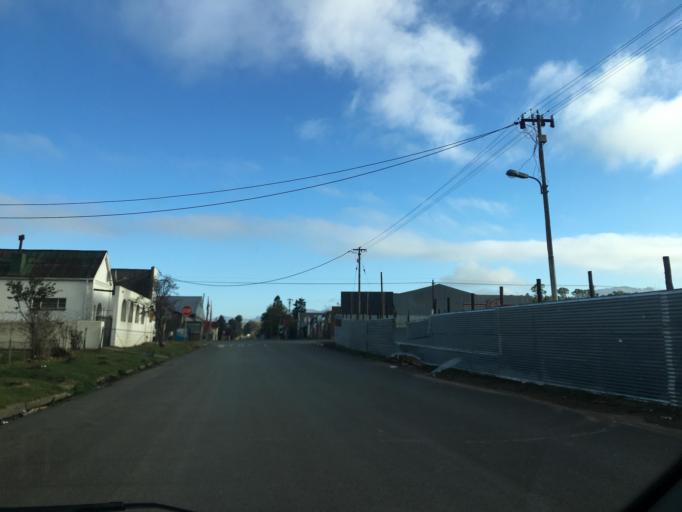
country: ZA
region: Eastern Cape
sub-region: Chris Hani District Municipality
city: Elliot
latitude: -31.3352
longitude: 27.8480
